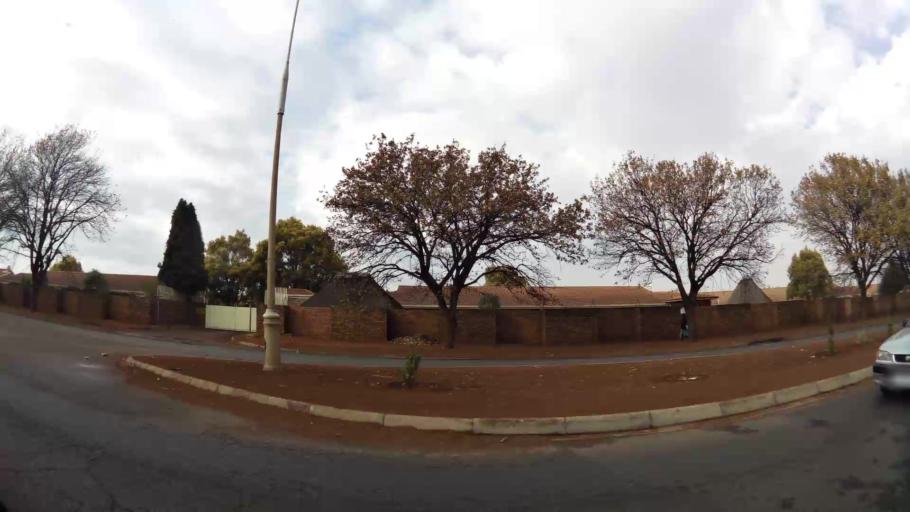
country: ZA
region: Gauteng
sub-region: Sedibeng District Municipality
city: Vanderbijlpark
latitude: -26.7046
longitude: 27.8266
